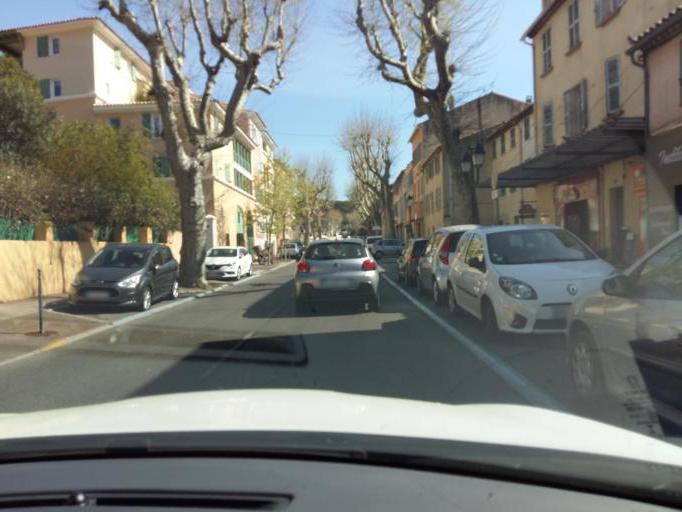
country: FR
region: Provence-Alpes-Cote d'Azur
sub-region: Departement du Var
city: Ollioules
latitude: 43.1378
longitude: 5.8495
